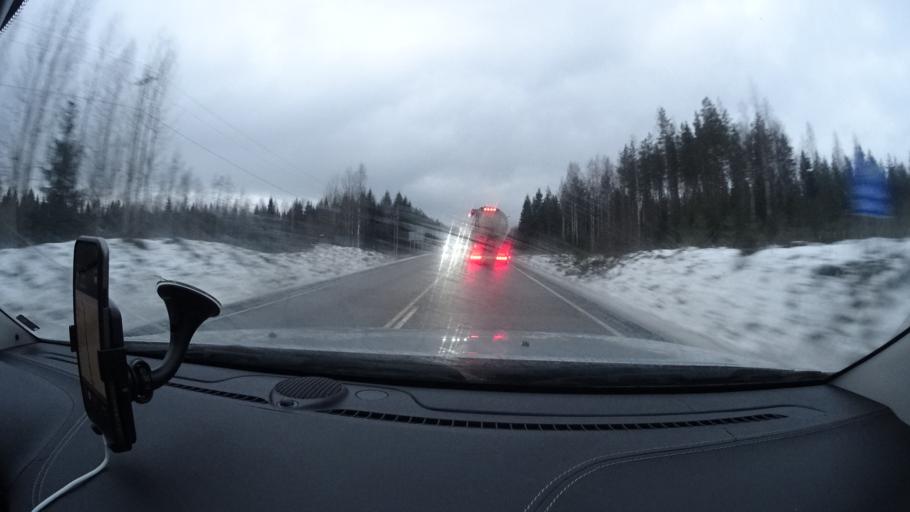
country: FI
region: Central Finland
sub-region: Joutsa
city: Leivonmaeki
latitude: 61.9534
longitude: 26.1052
